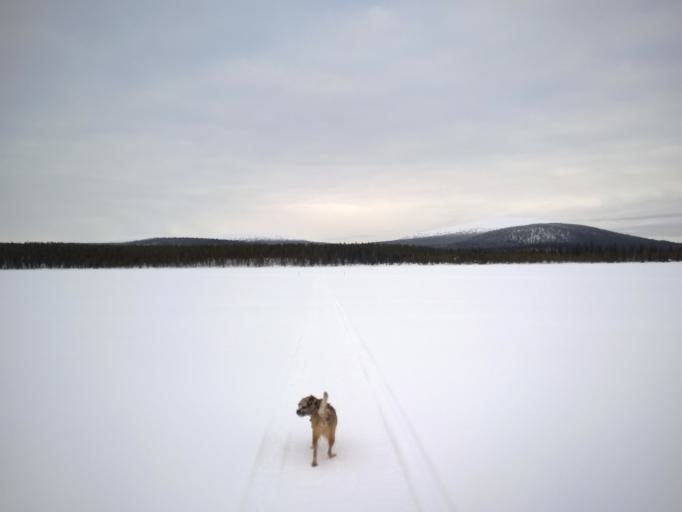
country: FI
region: Lapland
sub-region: Tunturi-Lappi
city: Muonio
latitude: 67.9358
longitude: 24.0338
